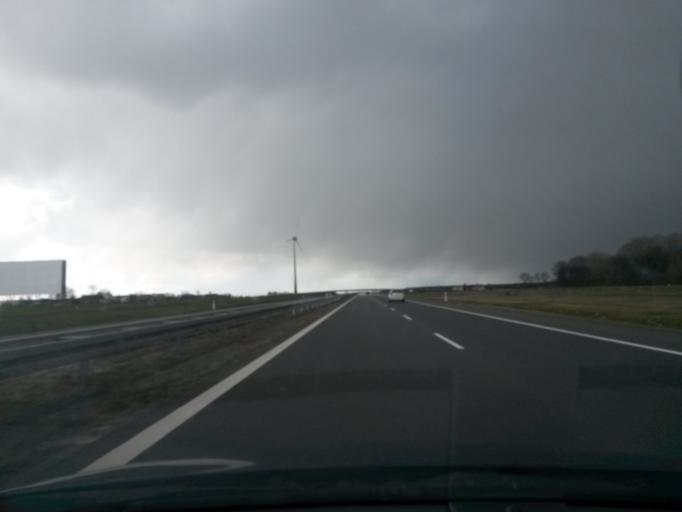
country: PL
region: Greater Poland Voivodeship
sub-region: Powiat sredzki
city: Dominowo
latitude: 52.3101
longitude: 17.2838
